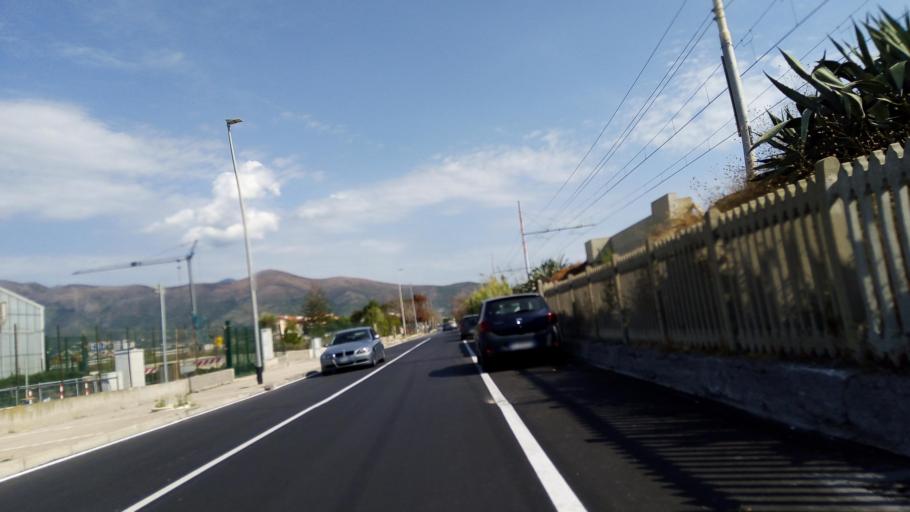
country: IT
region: Liguria
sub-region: Provincia di Savona
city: Albenga
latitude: 44.0667
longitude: 8.2250
